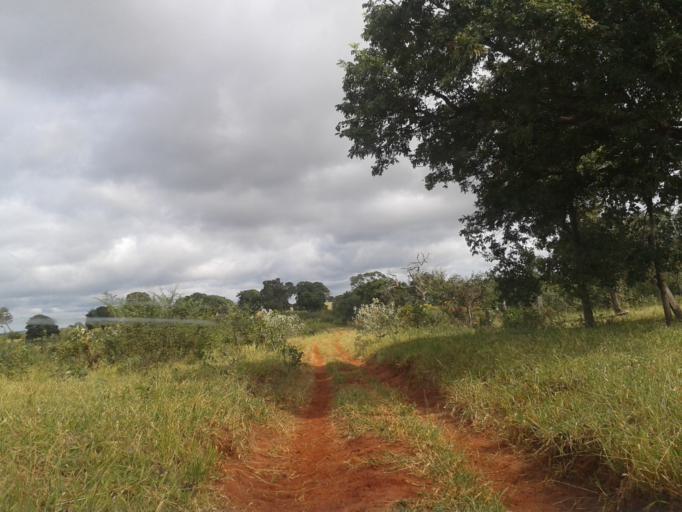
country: BR
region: Minas Gerais
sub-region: Campina Verde
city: Campina Verde
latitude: -19.4131
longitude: -49.6709
